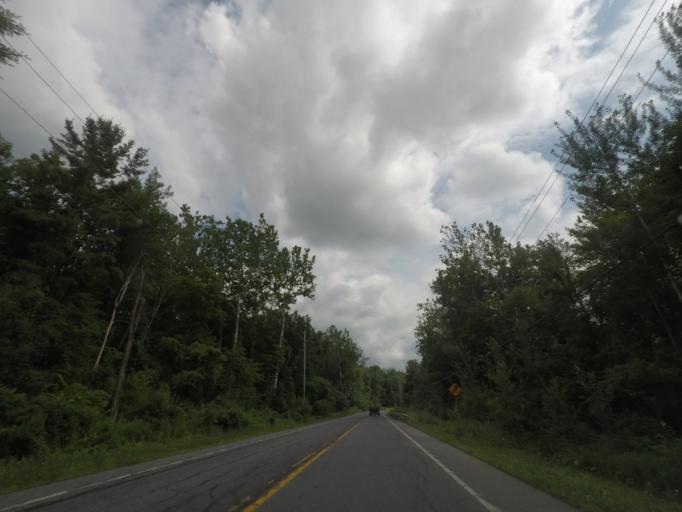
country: US
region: New York
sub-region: Saratoga County
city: Stillwater
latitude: 42.9159
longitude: -73.6290
